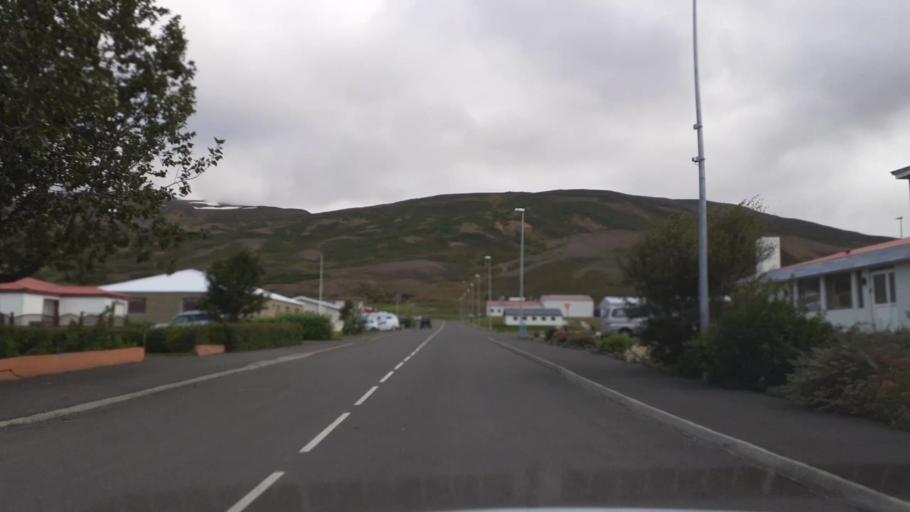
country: IS
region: Northeast
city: Akureyri
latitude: 65.9499
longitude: -18.1806
